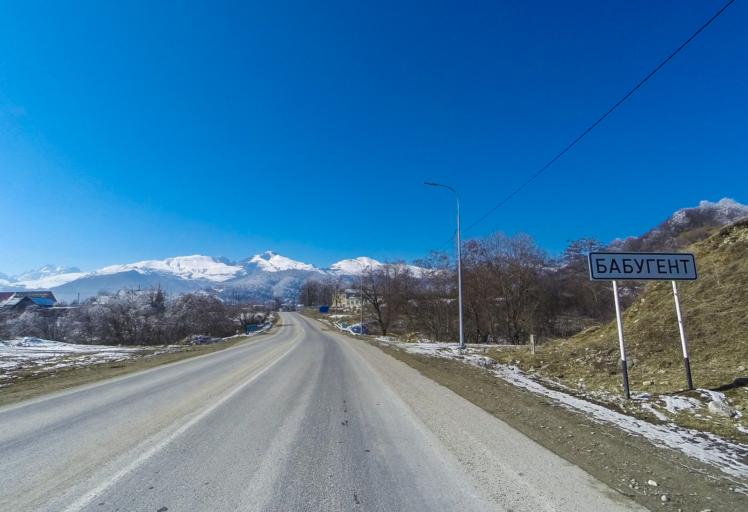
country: RU
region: Kabardino-Balkariya
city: Babugent
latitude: 43.2846
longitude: 43.5580
